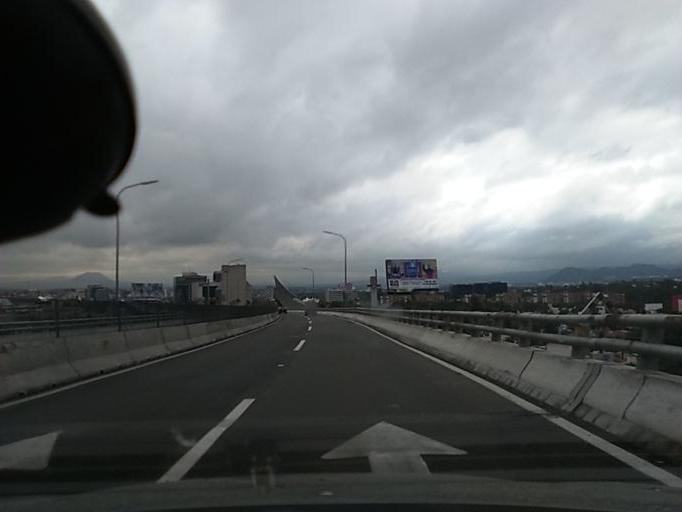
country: MX
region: Mexico City
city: Tlalpan
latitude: 19.3023
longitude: -99.1966
